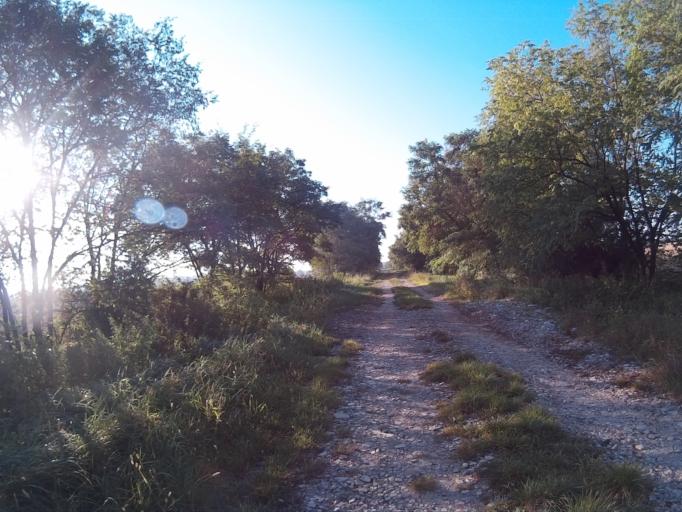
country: HU
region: Vas
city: Jak
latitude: 47.1287
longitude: 16.5870
